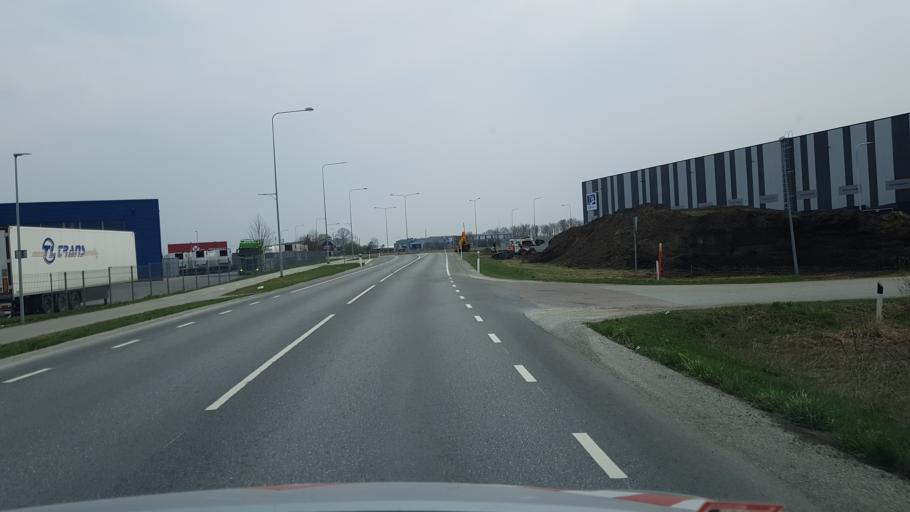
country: EE
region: Harju
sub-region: Rae vald
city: Jueri
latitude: 59.3676
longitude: 24.8702
